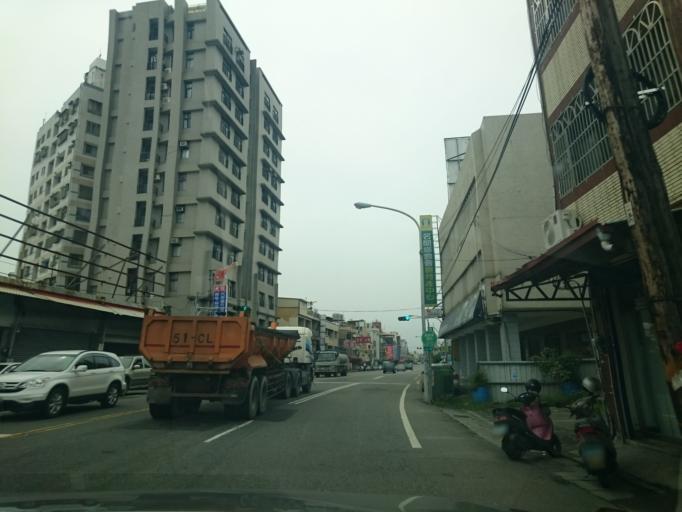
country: TW
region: Taiwan
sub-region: Nantou
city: Nantou
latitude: 23.8365
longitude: 120.7042
